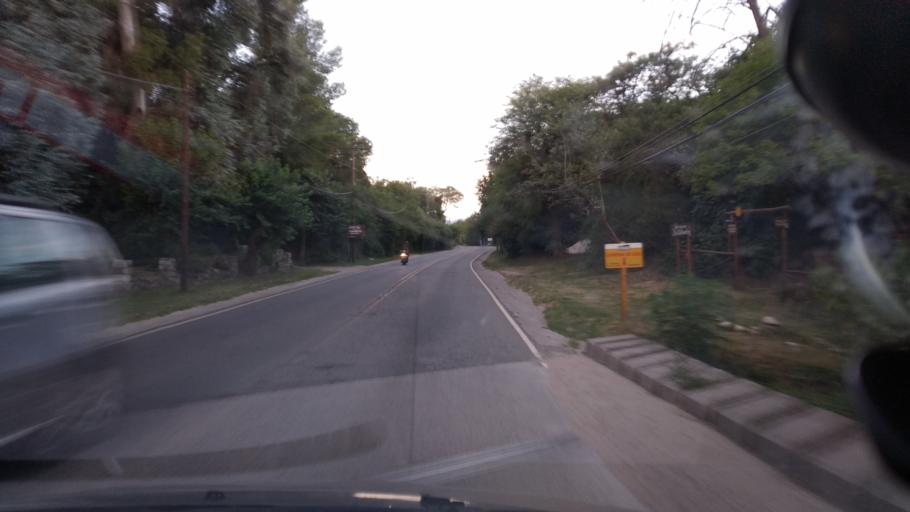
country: AR
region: Cordoba
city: Villa Las Rosas
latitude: -31.9553
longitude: -65.0634
